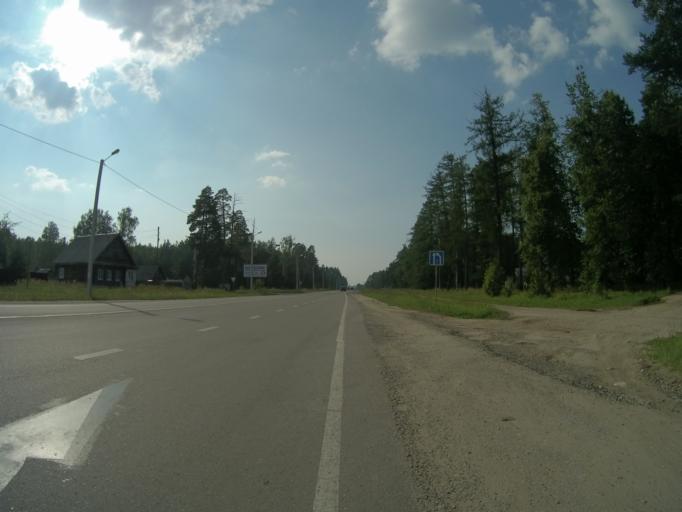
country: RU
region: Vladimir
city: Andreyevo
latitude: 55.9290
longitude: 41.1166
